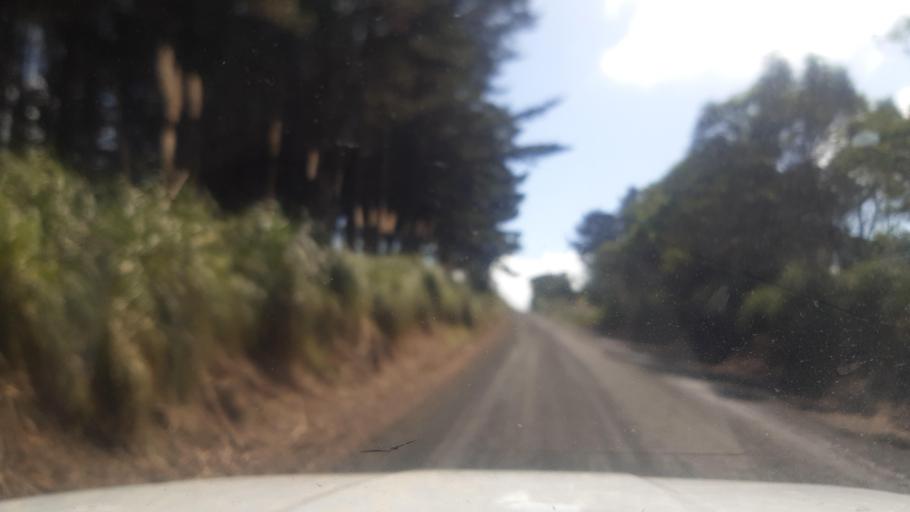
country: NZ
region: Northland
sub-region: Far North District
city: Kaitaia
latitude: -34.7527
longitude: 173.0651
